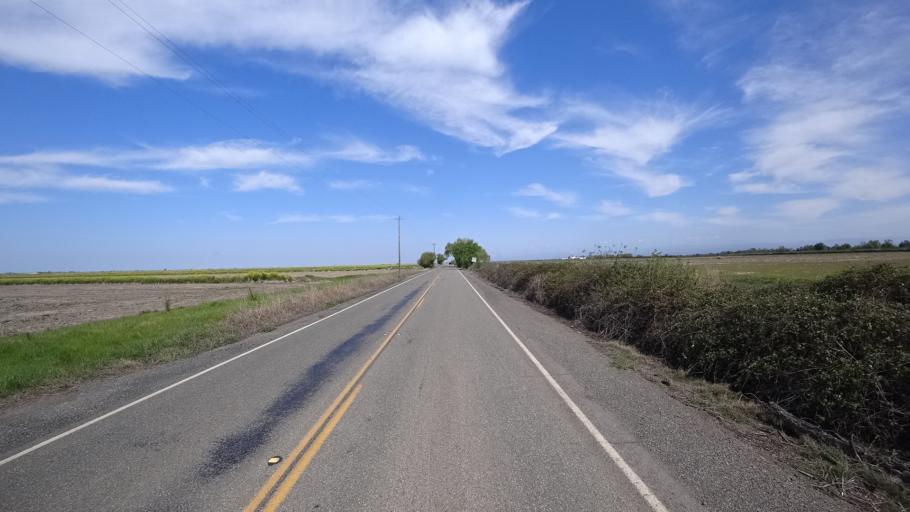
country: US
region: California
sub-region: Butte County
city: Durham
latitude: 39.5372
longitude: -121.8565
